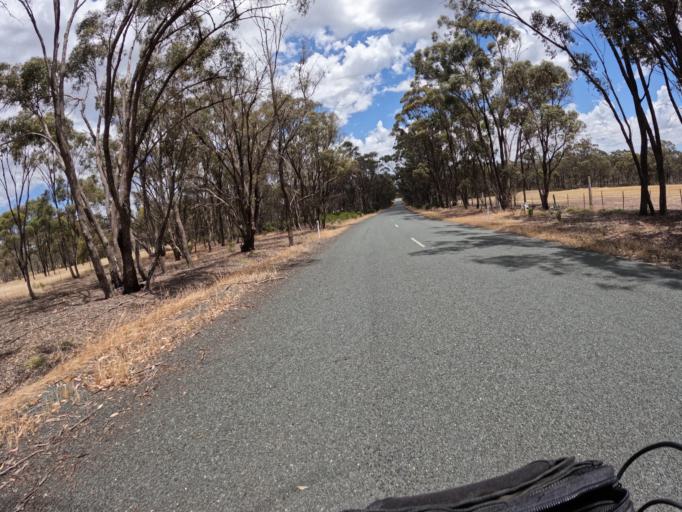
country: AU
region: Victoria
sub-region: Greater Shepparton
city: Shepparton
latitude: -36.6833
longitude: 145.1889
